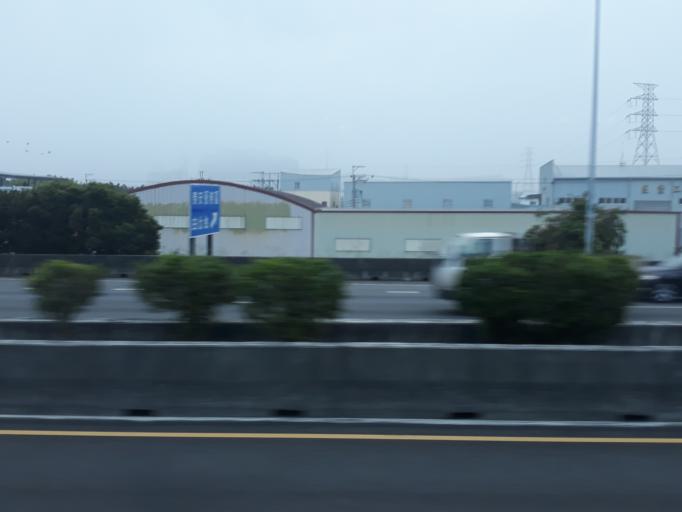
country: TW
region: Taiwan
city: Fengyuan
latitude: 24.3162
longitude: 120.7038
